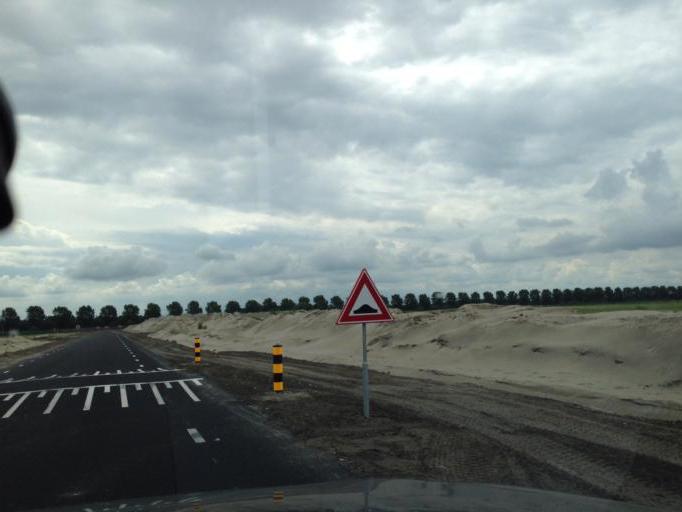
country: NL
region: Flevoland
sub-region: Gemeente Almere
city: Almere Stad
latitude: 52.3710
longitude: 5.2969
